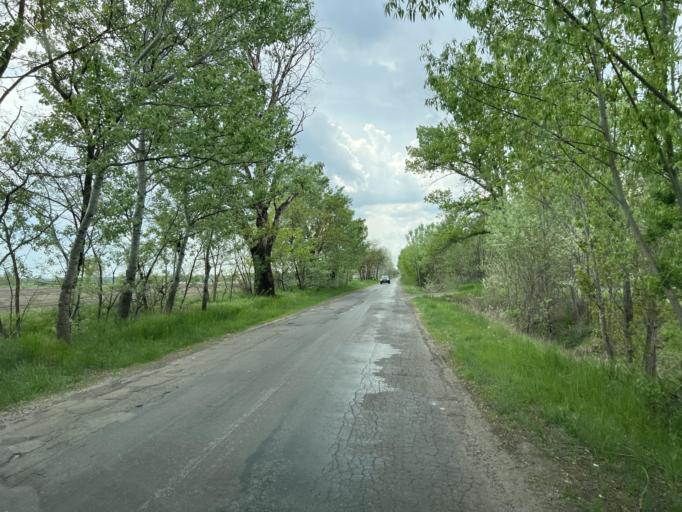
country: HU
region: Pest
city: Cegled
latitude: 47.1280
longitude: 19.7669
